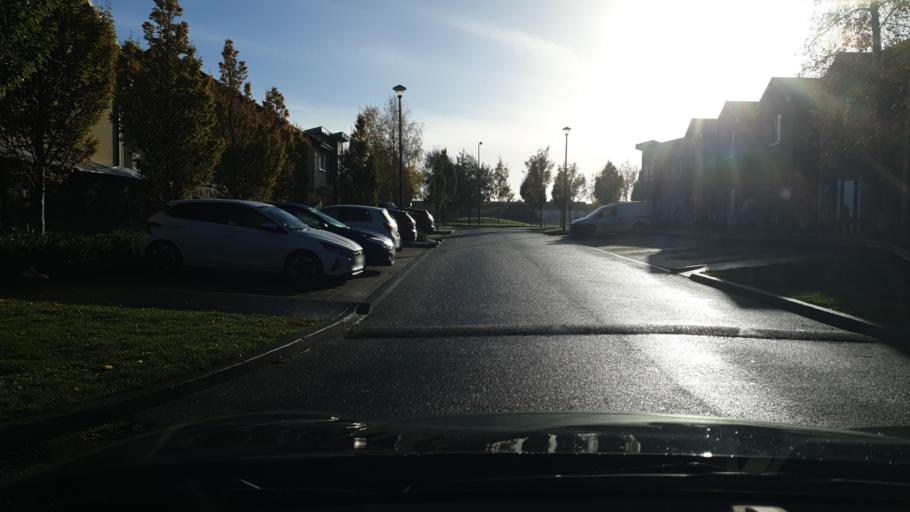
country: IE
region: Leinster
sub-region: An Mhi
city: Ashbourne
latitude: 53.5074
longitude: -6.4065
